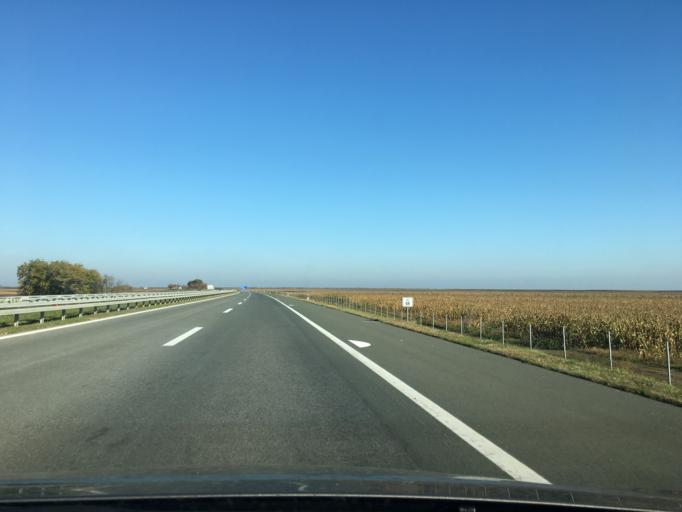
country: RS
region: Autonomna Pokrajina Vojvodina
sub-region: Severnobacki Okrug
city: Mali Igos
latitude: 45.6666
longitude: 19.7280
